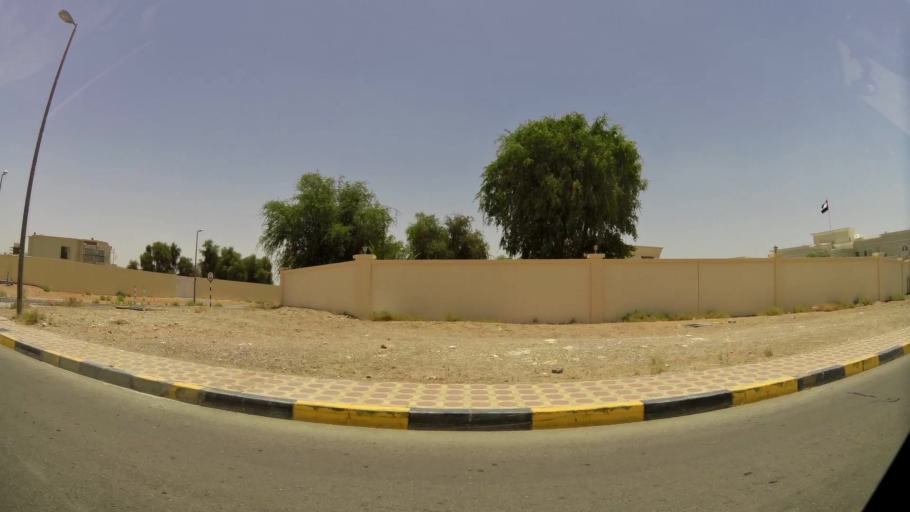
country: OM
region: Al Buraimi
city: Al Buraymi
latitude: 24.2820
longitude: 55.7324
